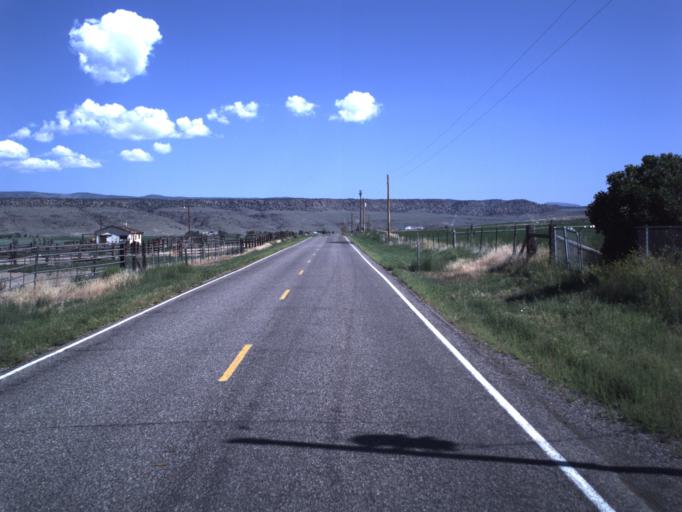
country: US
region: Utah
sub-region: Wayne County
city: Loa
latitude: 38.4238
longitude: -111.6202
